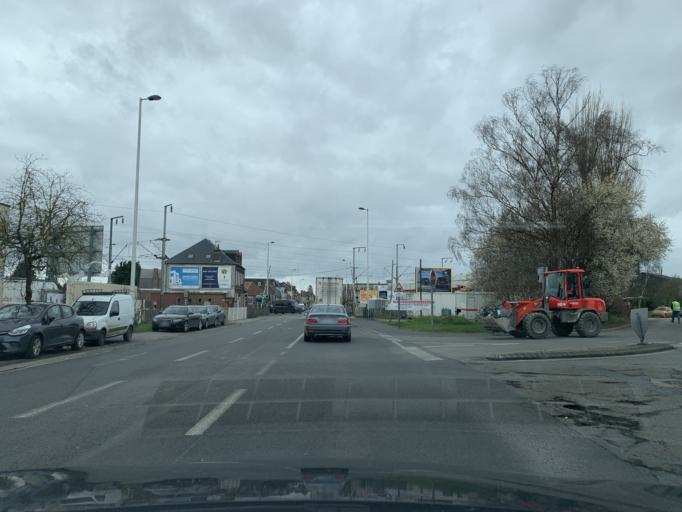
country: FR
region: Nord-Pas-de-Calais
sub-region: Departement du Nord
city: Cambrai
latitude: 50.1705
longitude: 3.2586
